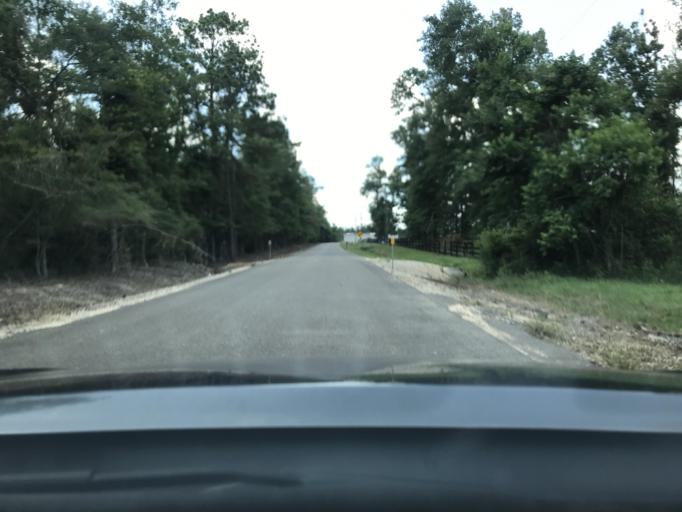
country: US
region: Louisiana
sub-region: Calcasieu Parish
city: Moss Bluff
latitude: 30.3335
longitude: -93.1308
